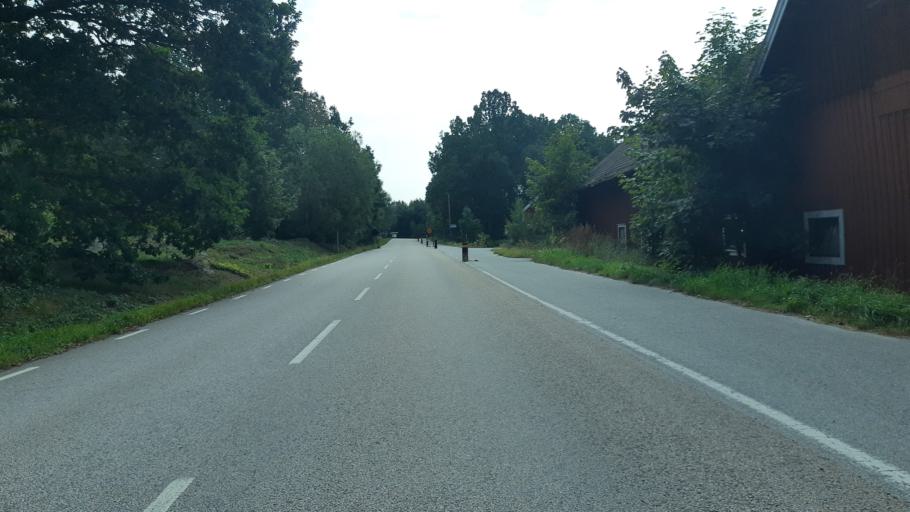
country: SE
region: Blekinge
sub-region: Karlskrona Kommun
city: Nattraby
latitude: 56.2227
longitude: 15.4134
